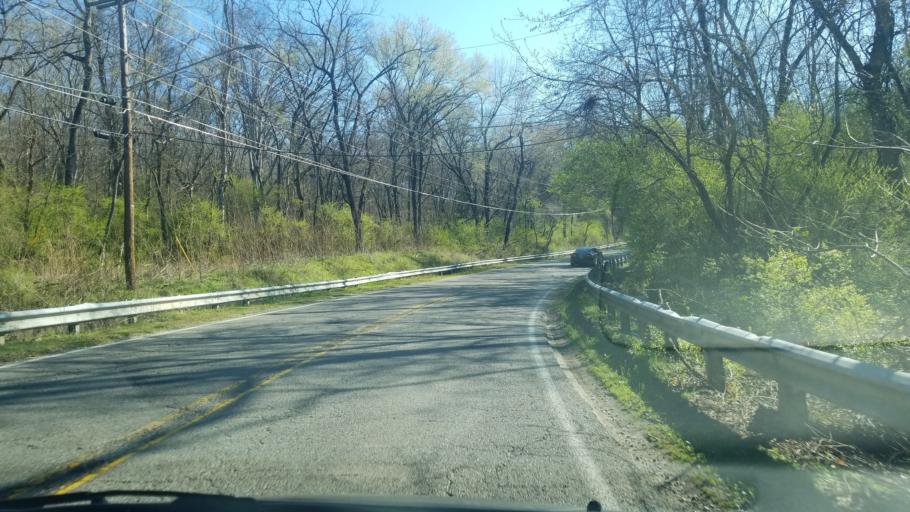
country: US
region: Tennessee
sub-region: Hamilton County
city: East Chattanooga
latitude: 35.1140
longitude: -85.2165
